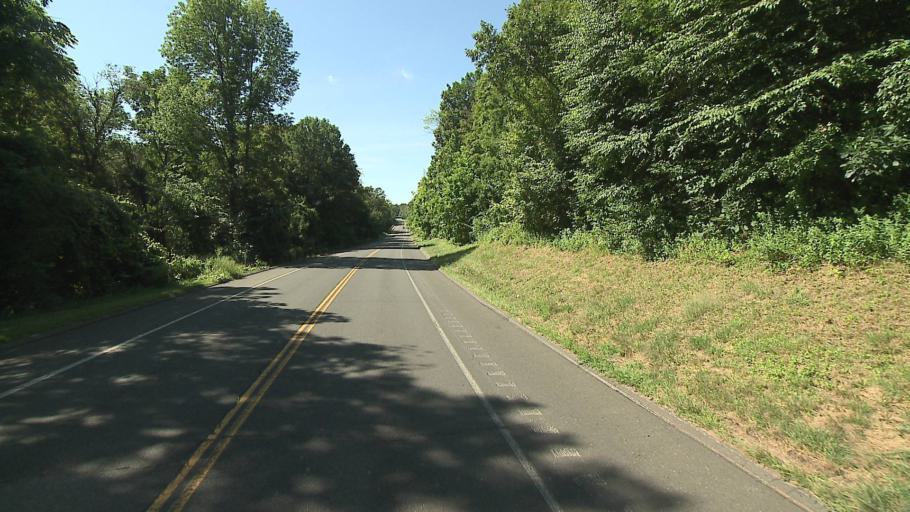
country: US
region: Connecticut
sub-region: Hartford County
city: Tariffville
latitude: 41.9002
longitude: -72.7475
